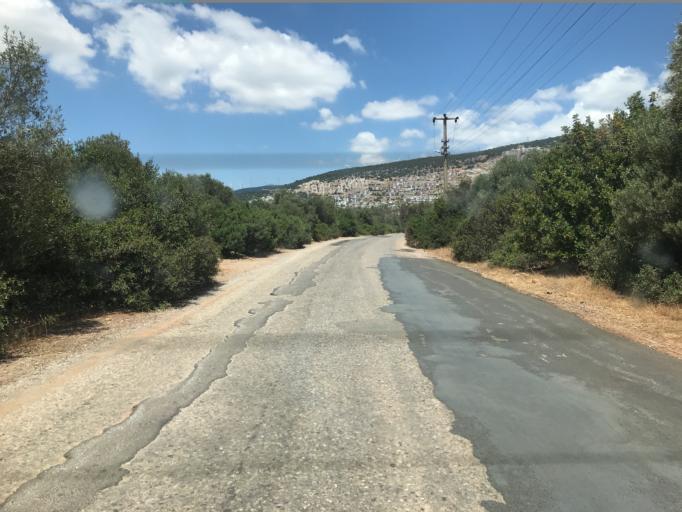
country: TR
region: Aydin
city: Sarikemer
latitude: 37.4110
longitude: 27.4231
